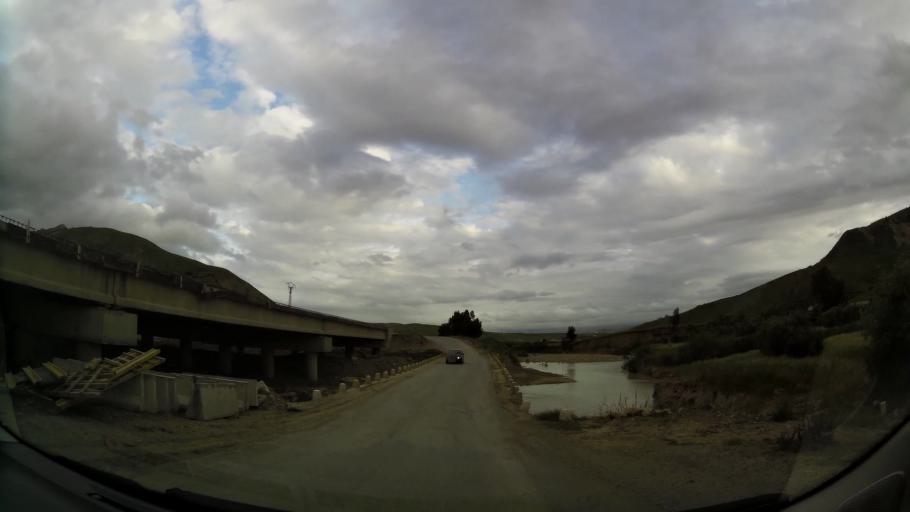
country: MA
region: Taza-Al Hoceima-Taounate
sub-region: Taza
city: Taza
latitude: 34.2914
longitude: -3.9682
